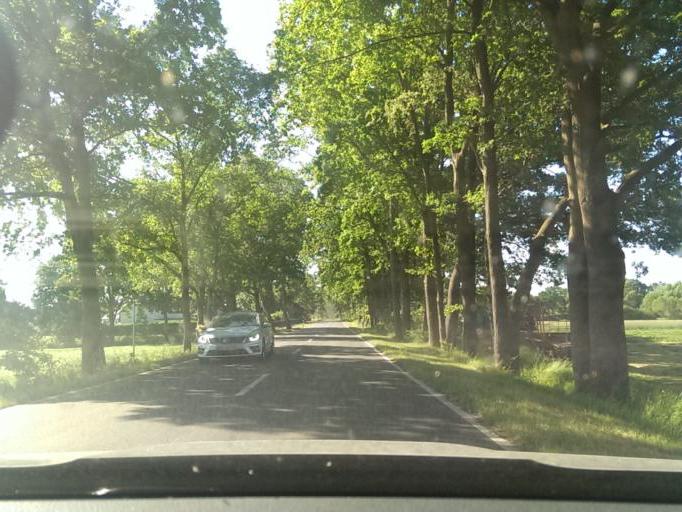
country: DE
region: Lower Saxony
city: Elze
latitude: 52.5557
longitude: 9.7377
